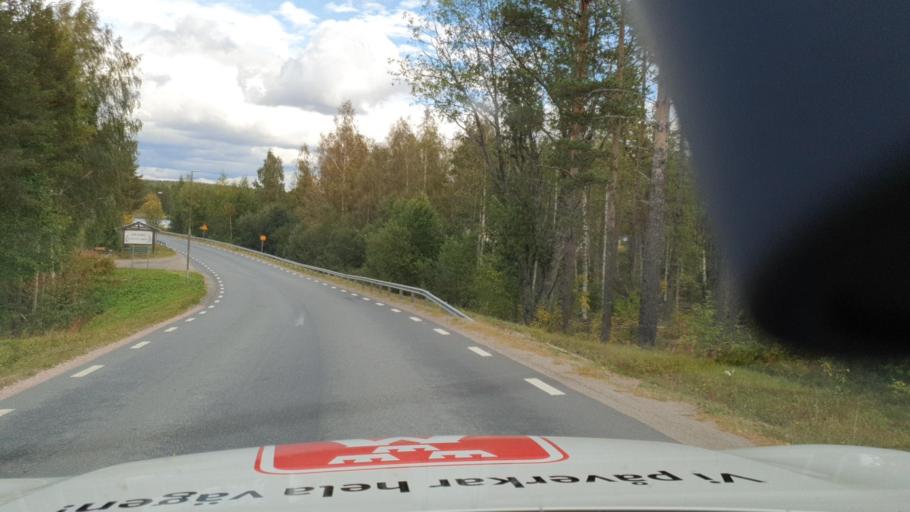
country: NO
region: Hedmark
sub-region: Trysil
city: Innbygda
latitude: 61.6890
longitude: 13.1692
